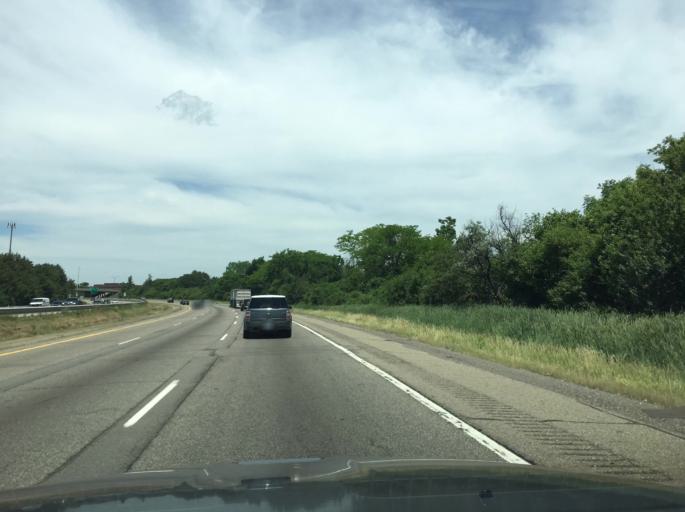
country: US
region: Michigan
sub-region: Oakland County
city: Troy
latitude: 42.6020
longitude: -83.1642
